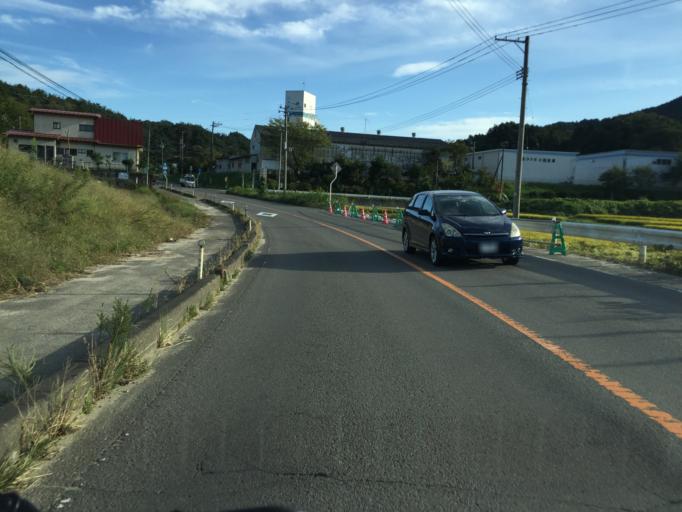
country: JP
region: Fukushima
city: Hobaramachi
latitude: 37.7665
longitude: 140.5954
